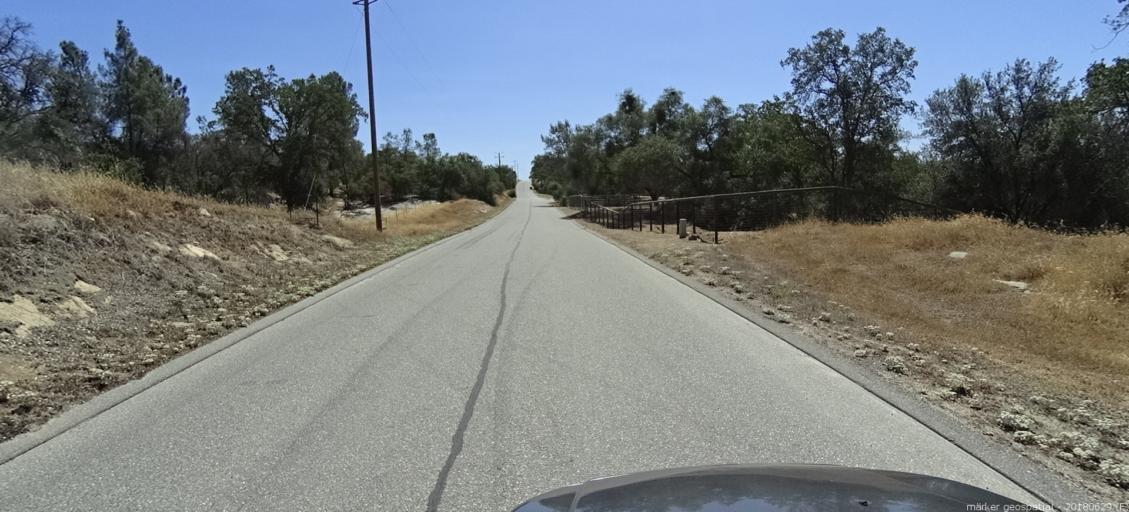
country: US
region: California
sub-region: Madera County
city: Yosemite Lakes
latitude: 37.1634
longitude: -119.7636
